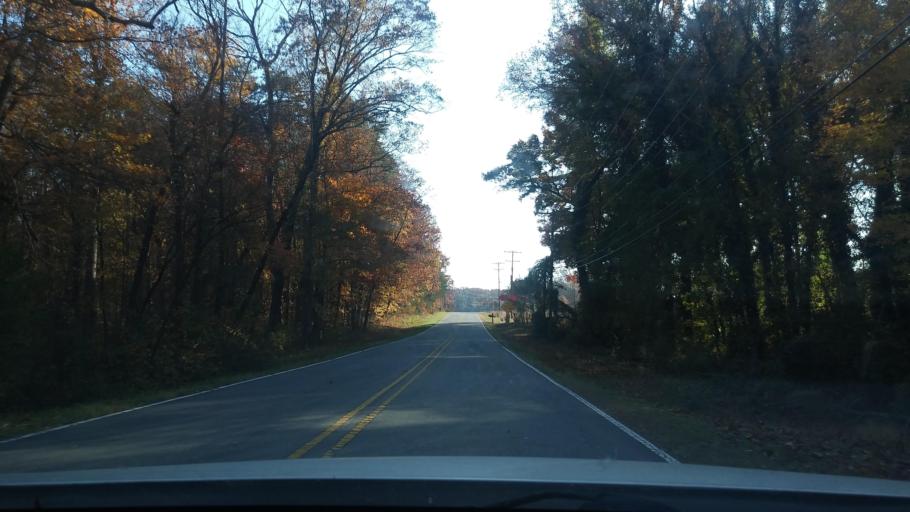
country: US
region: North Carolina
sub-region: Rockingham County
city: Reidsville
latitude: 36.2934
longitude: -79.7345
